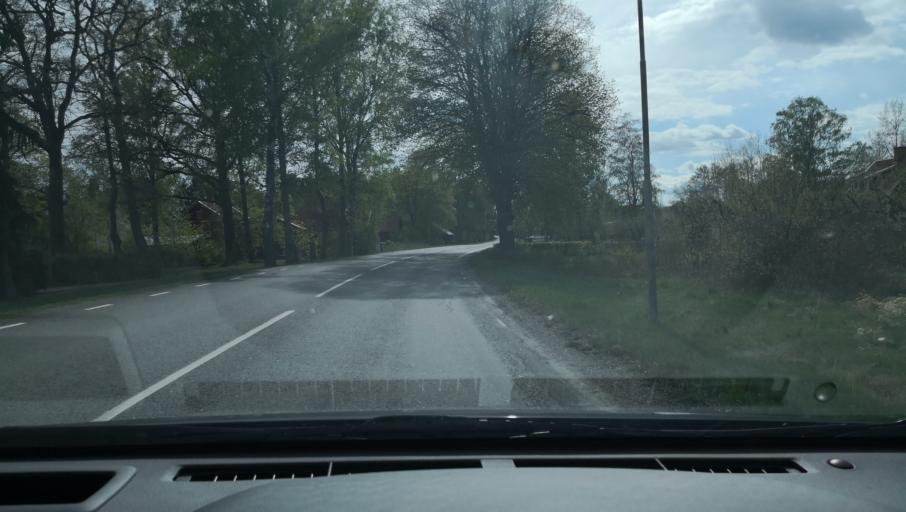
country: SE
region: OErebro
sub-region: Hallsbergs Kommun
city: Hallsberg
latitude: 59.0805
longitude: 15.1538
